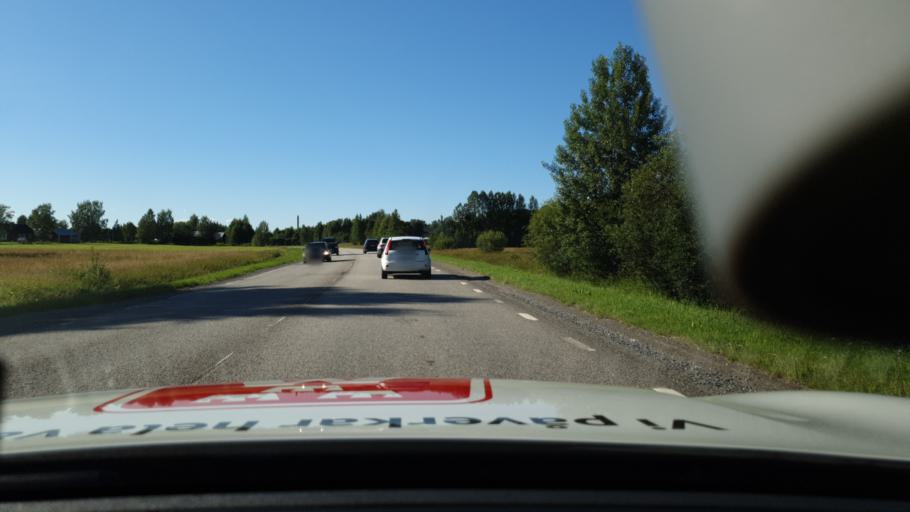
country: SE
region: Norrbotten
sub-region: Lulea Kommun
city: Sodra Sunderbyn
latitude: 65.5522
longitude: 21.8420
